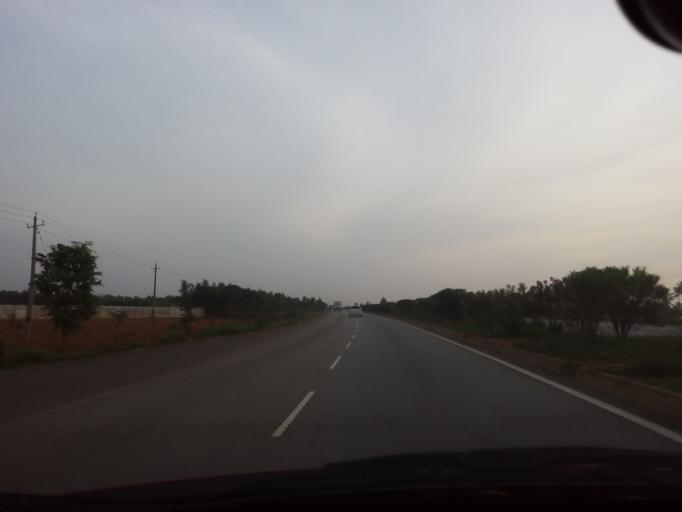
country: IN
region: Karnataka
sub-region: Chikkaballapur
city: Chik Ballapur
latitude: 13.3965
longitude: 77.7418
